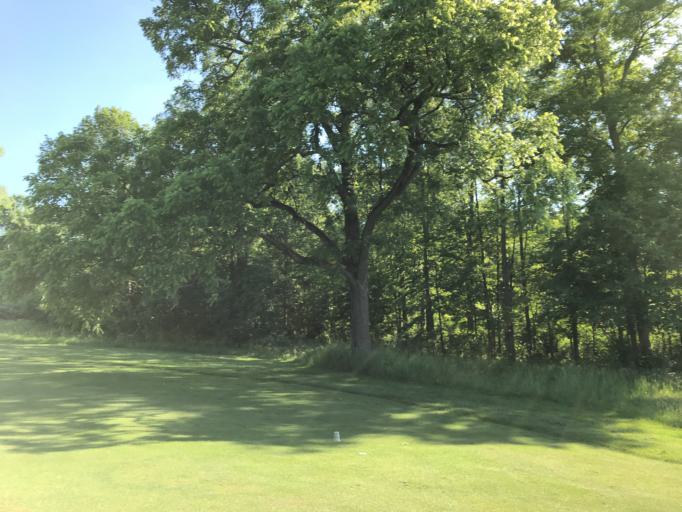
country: US
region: Michigan
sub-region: Oakland County
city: South Lyon
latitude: 42.4419
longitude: -83.6117
